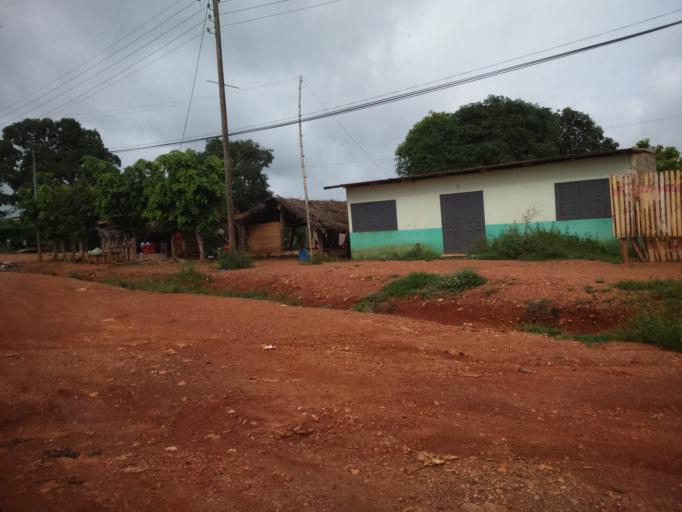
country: CI
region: Moyen-Comoe
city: Abengourou
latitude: 6.7192
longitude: -3.5153
